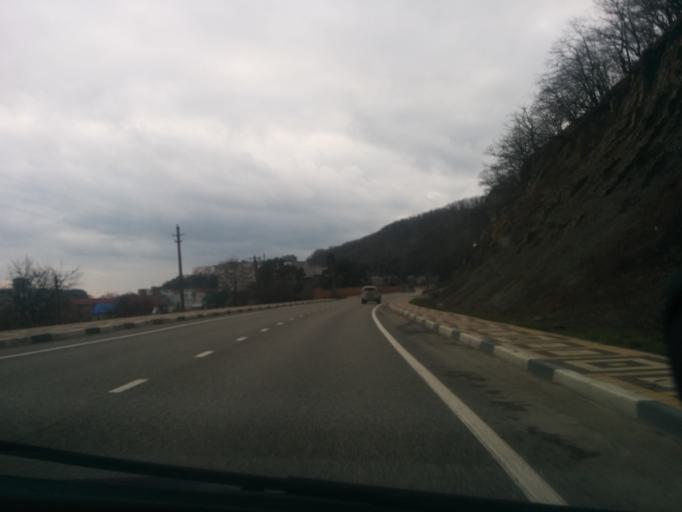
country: RU
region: Krasnodarskiy
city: Ol'ginka
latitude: 44.2065
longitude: 38.8906
